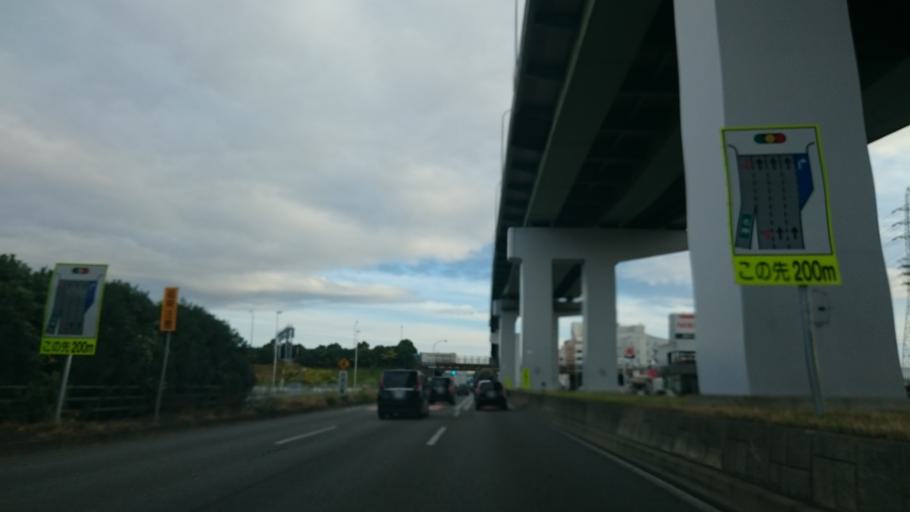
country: JP
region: Aichi
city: Komaki
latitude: 35.3015
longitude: 136.9095
